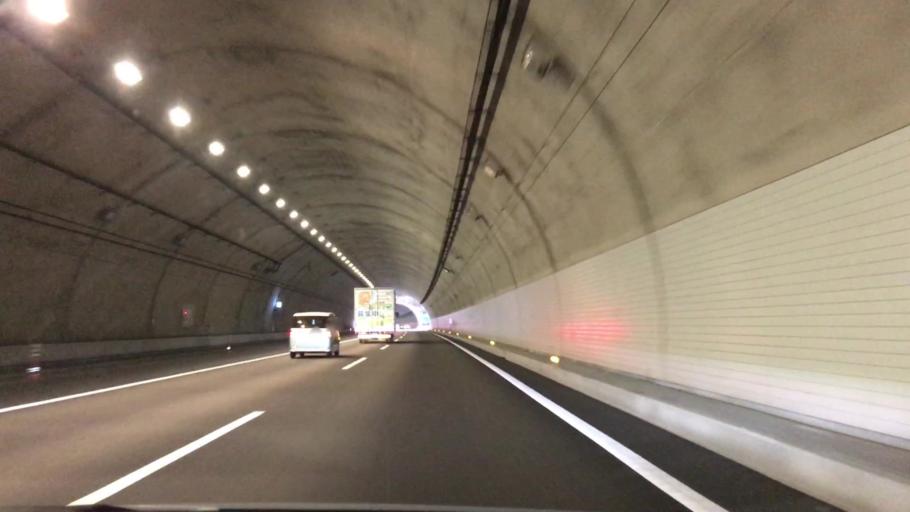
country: JP
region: Shizuoka
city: Shimada
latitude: 34.8708
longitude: 138.1661
